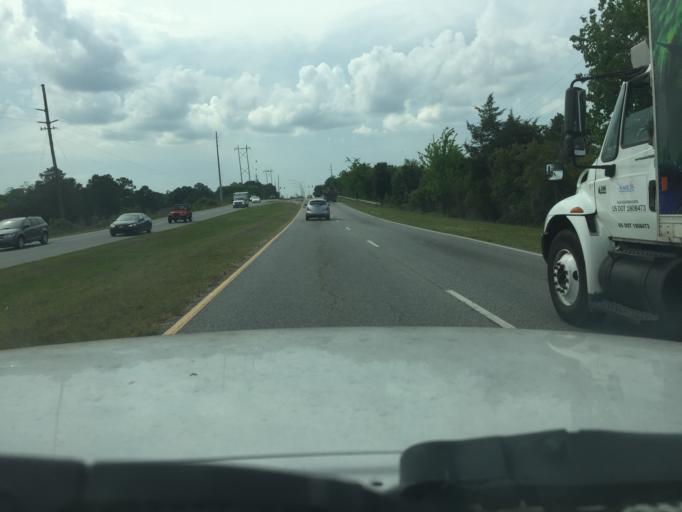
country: US
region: Georgia
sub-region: Chatham County
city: Whitemarsh Island
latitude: 32.0600
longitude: -81.0252
